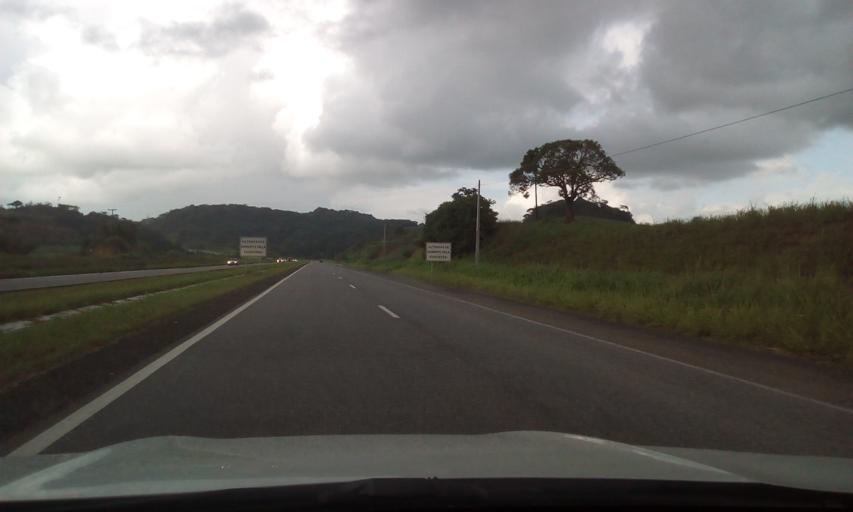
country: BR
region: Pernambuco
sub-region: Cabo De Santo Agostinho
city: Cabo
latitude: -8.2567
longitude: -35.0392
